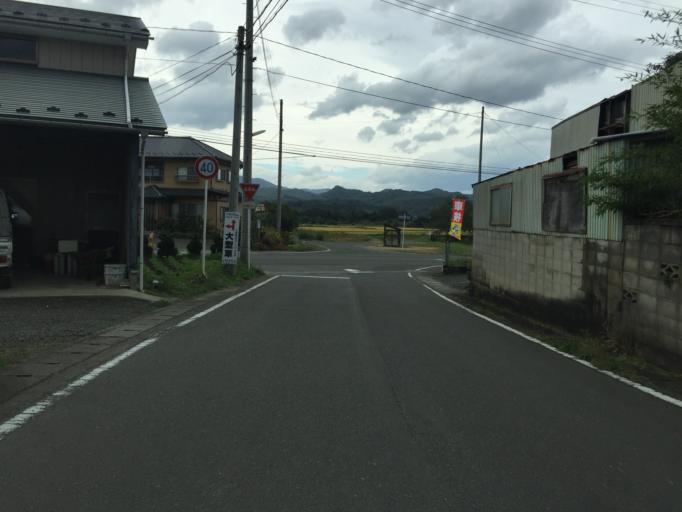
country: JP
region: Fukushima
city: Yanagawamachi-saiwaicho
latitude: 37.8641
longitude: 140.6163
